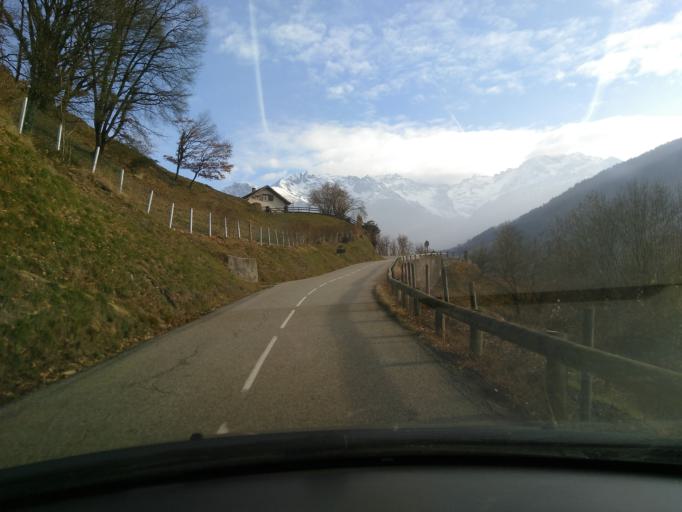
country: FR
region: Rhone-Alpes
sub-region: Departement de l'Isere
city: Villard-Bonnot
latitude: 45.2428
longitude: 5.9074
